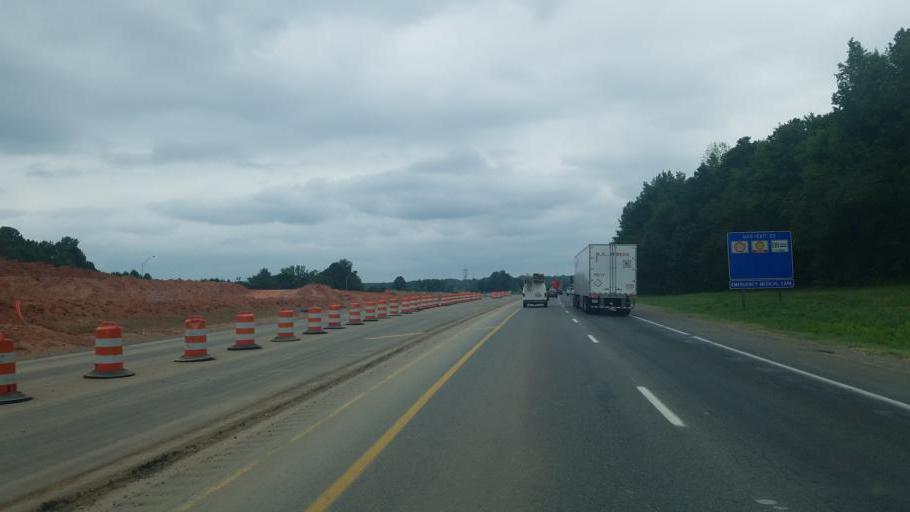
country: US
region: North Carolina
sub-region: Mecklenburg County
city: Huntersville
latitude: 35.4343
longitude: -80.8679
